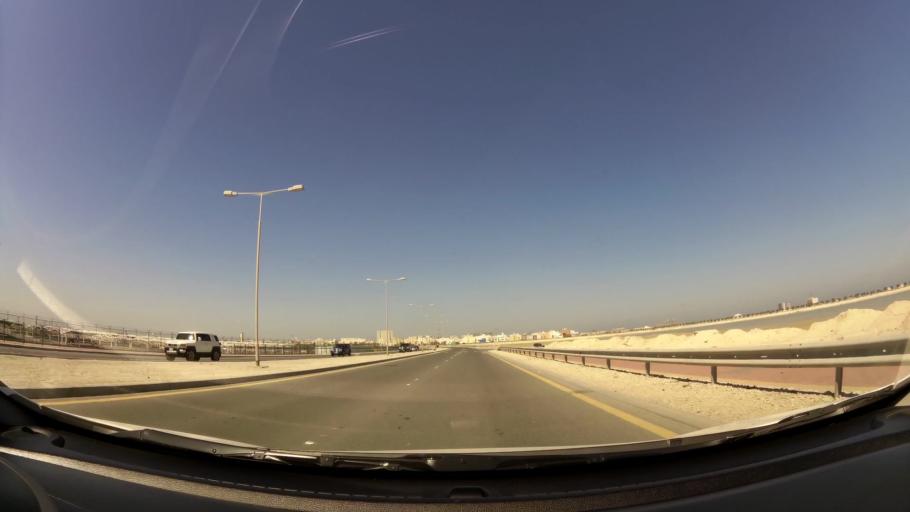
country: BH
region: Muharraq
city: Al Hadd
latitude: 26.2566
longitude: 50.6555
